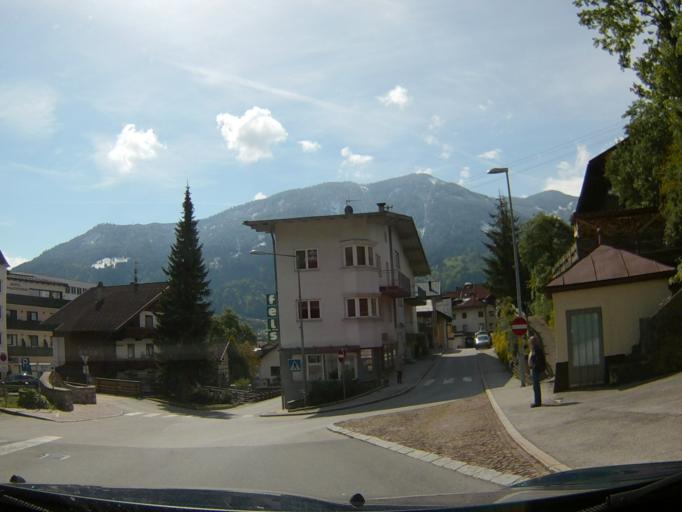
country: AT
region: Tyrol
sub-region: Politischer Bezirk Schwaz
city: Jenbach
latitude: 47.3930
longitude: 11.7719
